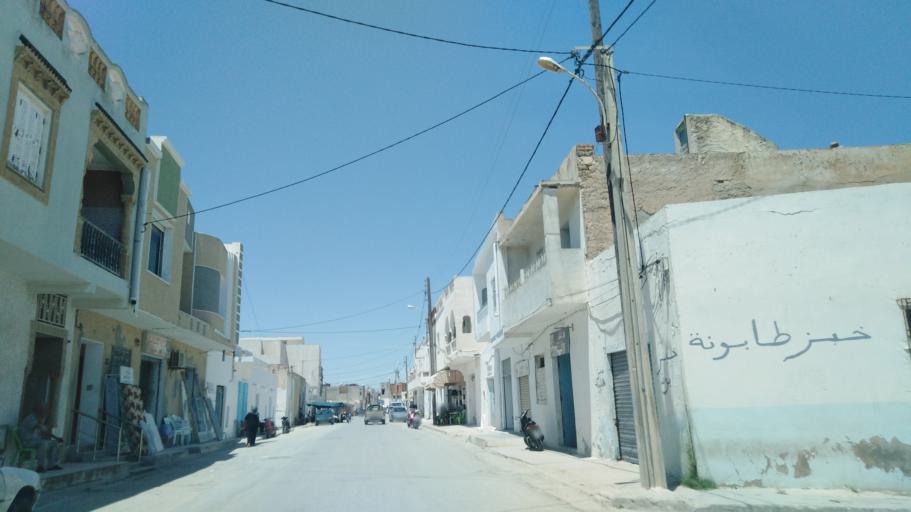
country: TN
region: Al Mahdiyah
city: Ksour Essaf
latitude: 35.4172
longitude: 10.9860
